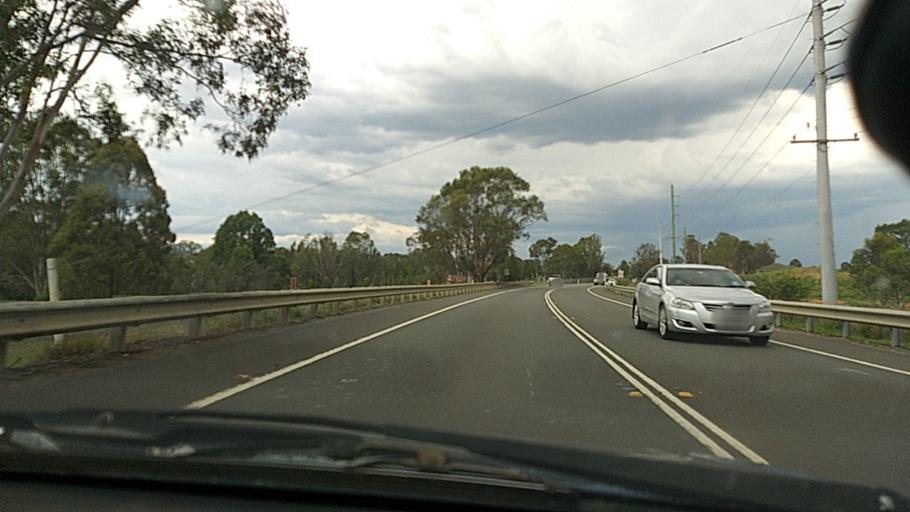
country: AU
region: New South Wales
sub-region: Penrith Municipality
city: Glenmore Park
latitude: -33.8089
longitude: 150.6949
